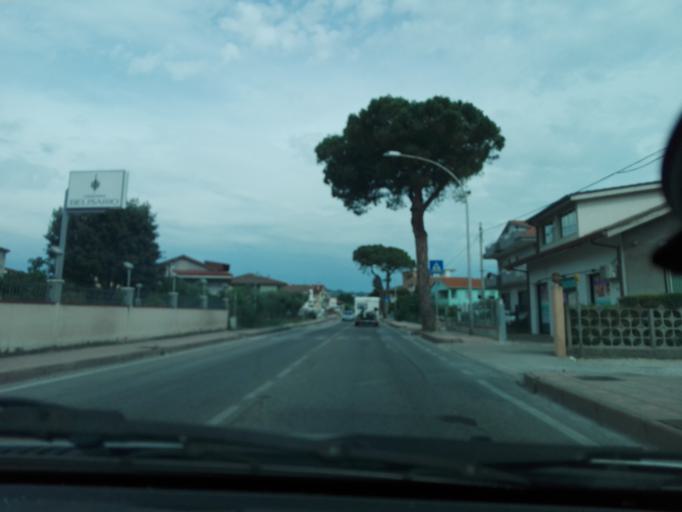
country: IT
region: Abruzzo
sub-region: Provincia di Pescara
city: San Martino Bassa
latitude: 42.5280
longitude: 14.1360
